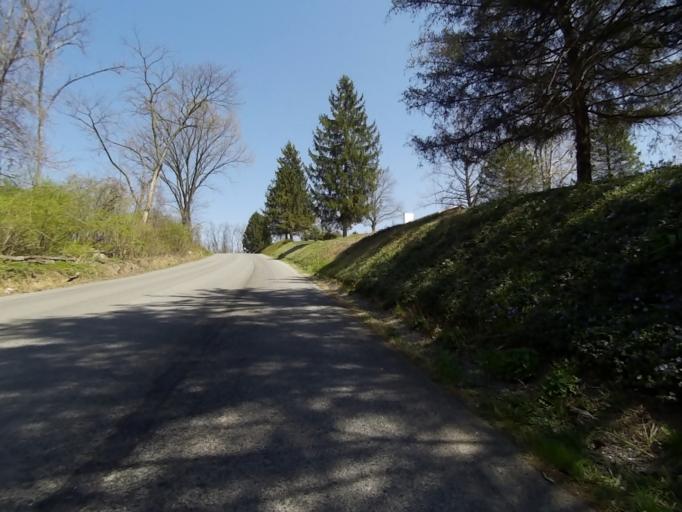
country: US
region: Pennsylvania
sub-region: Blair County
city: Williamsburg
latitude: 40.4781
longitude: -78.1910
